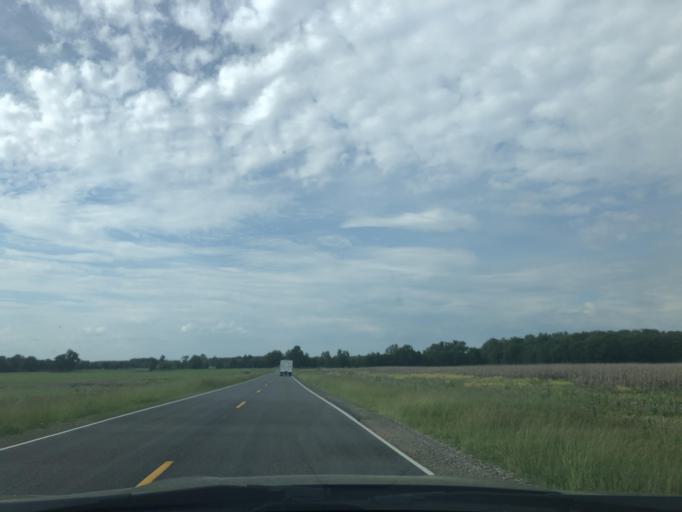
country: US
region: Michigan
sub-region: Clinton County
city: Saint Johns
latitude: 42.9598
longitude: -84.4837
